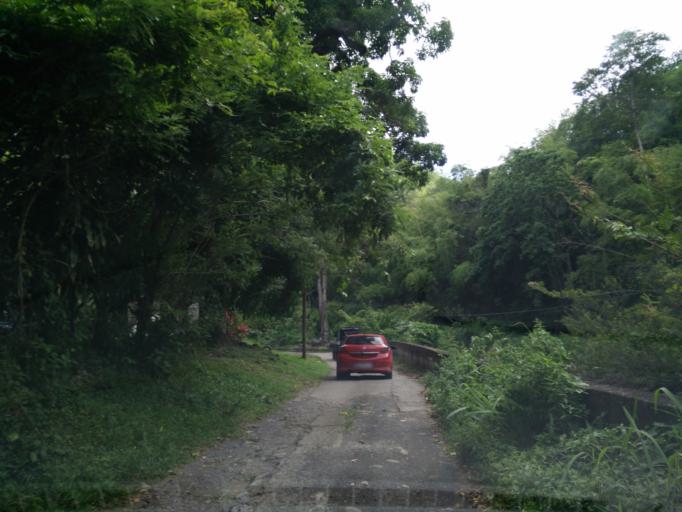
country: MQ
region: Martinique
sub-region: Martinique
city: Saint-Pierre
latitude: 14.7179
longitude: -61.1609
